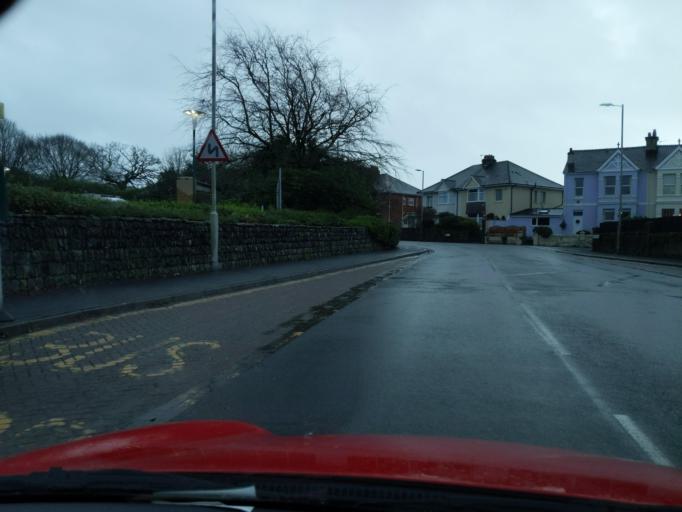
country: GB
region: England
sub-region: Plymouth
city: Plymouth
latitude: 50.3964
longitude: -4.1412
